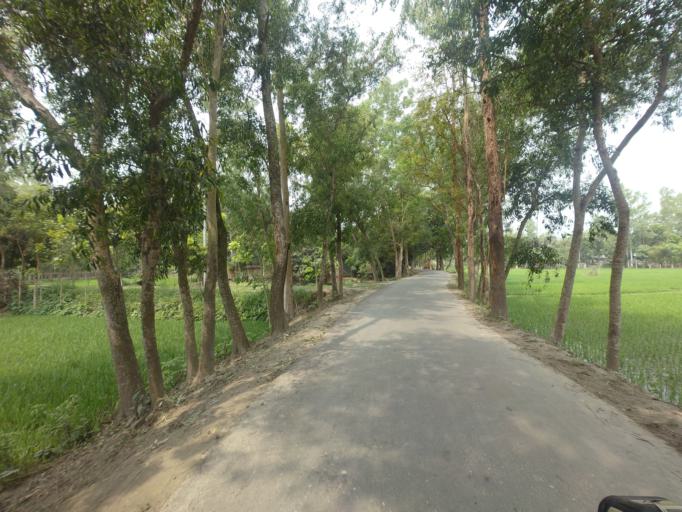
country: BD
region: Rajshahi
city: Sirajganj
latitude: 24.3490
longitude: 89.6775
